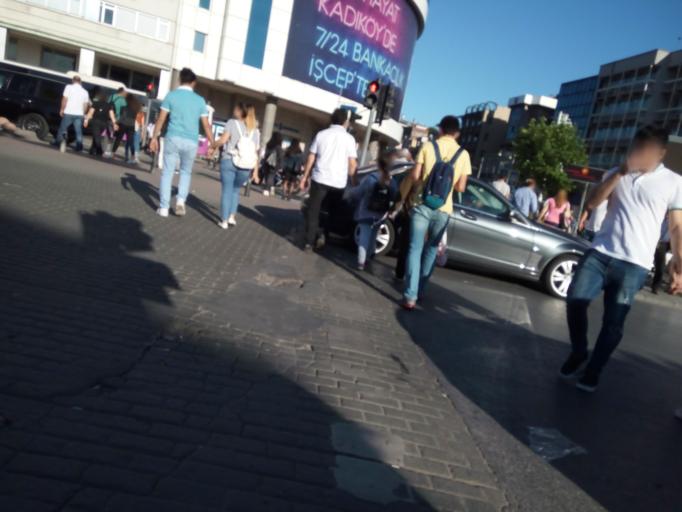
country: TR
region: Istanbul
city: UEskuedar
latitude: 40.9919
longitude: 29.0241
